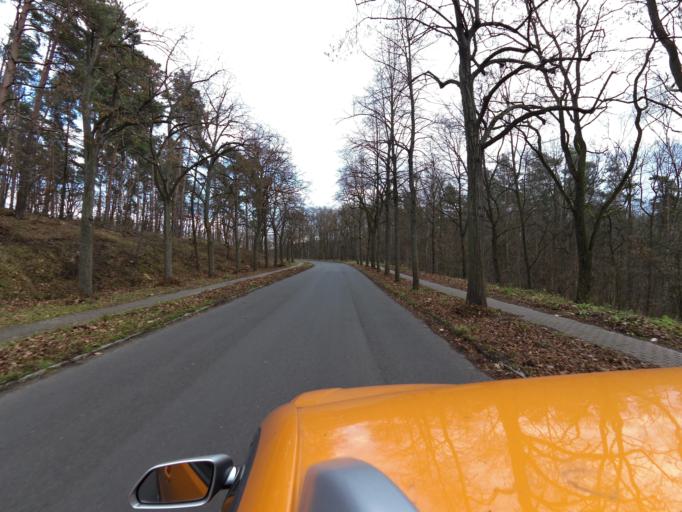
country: DE
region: Berlin
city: Gatow
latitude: 52.5004
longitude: 13.2206
